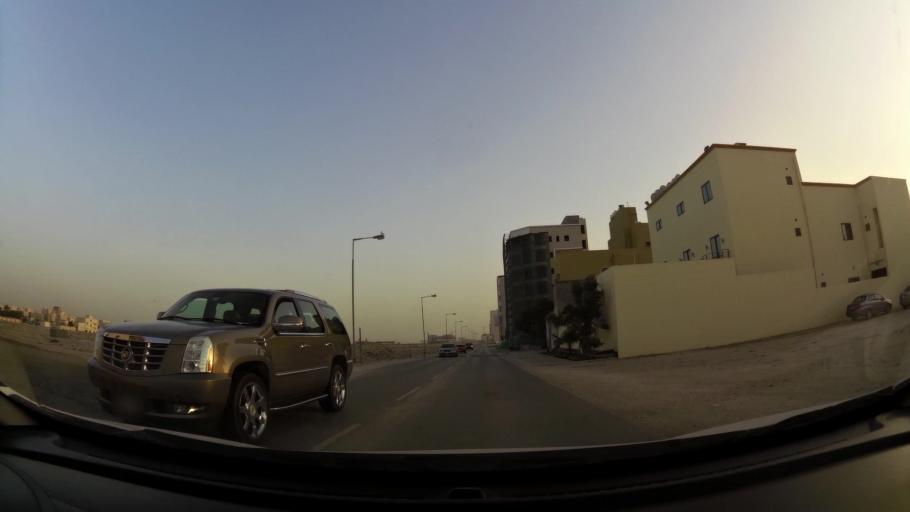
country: BH
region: Northern
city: Madinat `Isa
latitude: 26.1899
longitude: 50.4820
